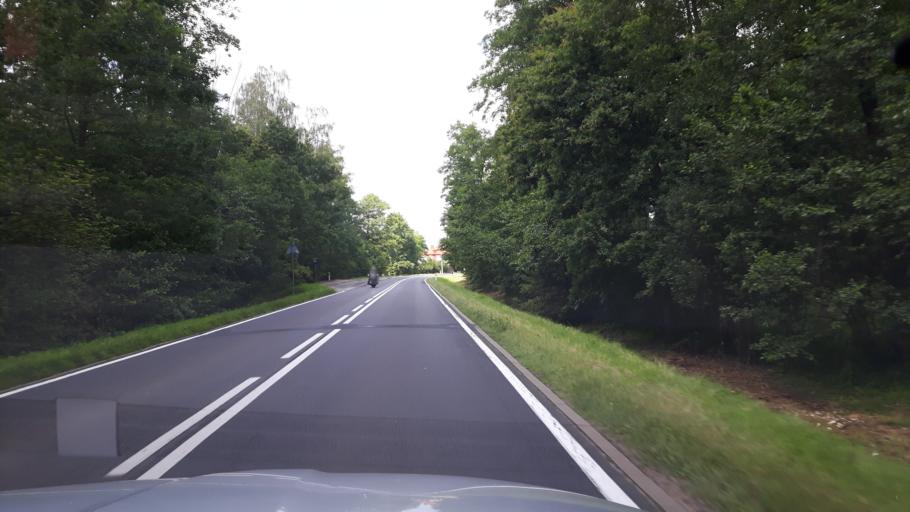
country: PL
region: Masovian Voivodeship
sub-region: Powiat ostrowski
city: Brok
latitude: 52.6987
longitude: 21.9198
